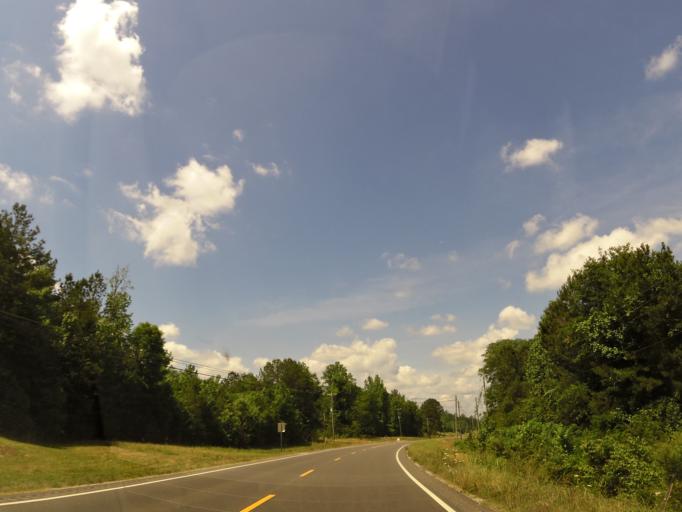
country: US
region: Alabama
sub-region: Lamar County
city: Sulligent
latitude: 33.9259
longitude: -88.0280
